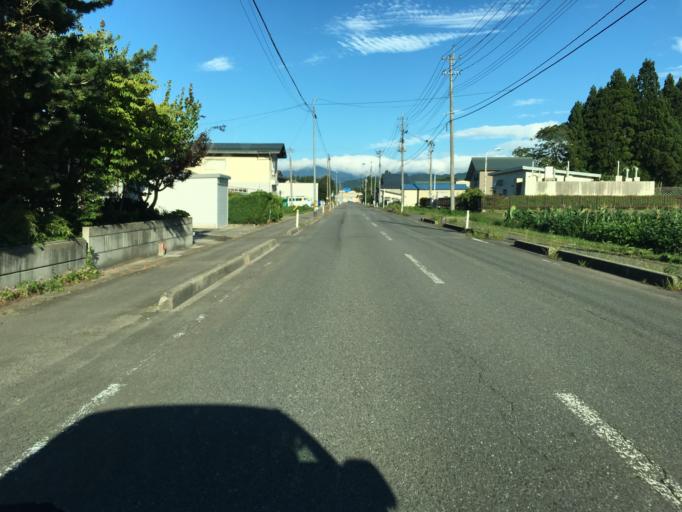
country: JP
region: Yamagata
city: Yonezawa
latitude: 37.8797
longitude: 140.1005
